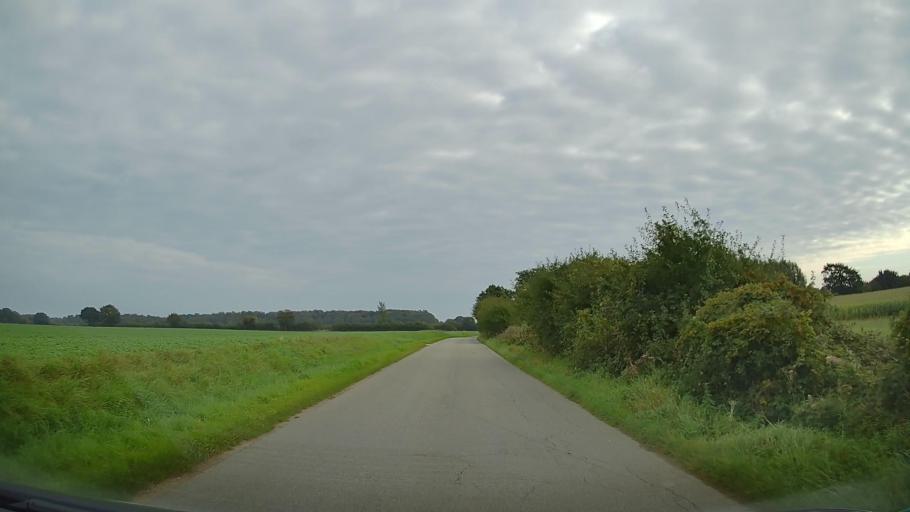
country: DE
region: Schleswig-Holstein
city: Panker
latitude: 54.3528
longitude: 10.5638
